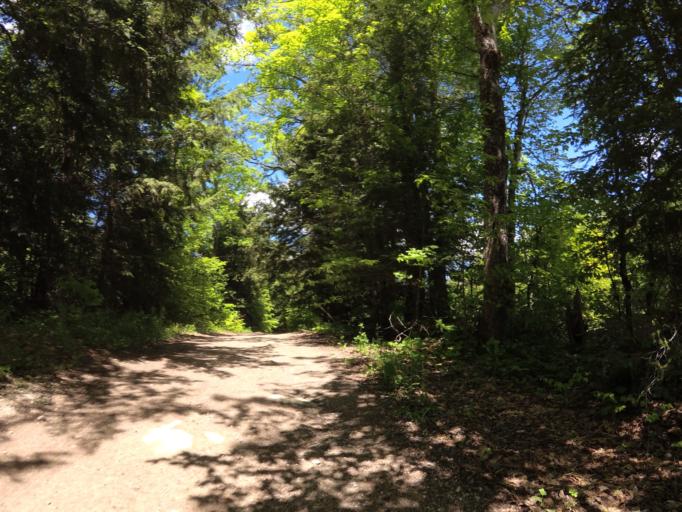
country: CA
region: Ontario
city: Renfrew
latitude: 45.0155
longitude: -76.8944
